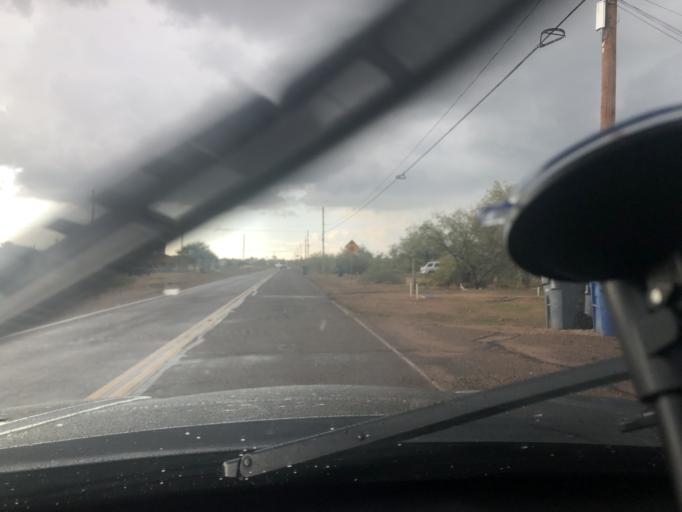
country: US
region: Arizona
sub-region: Maricopa County
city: Scottsdale
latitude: 33.4877
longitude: -111.8807
